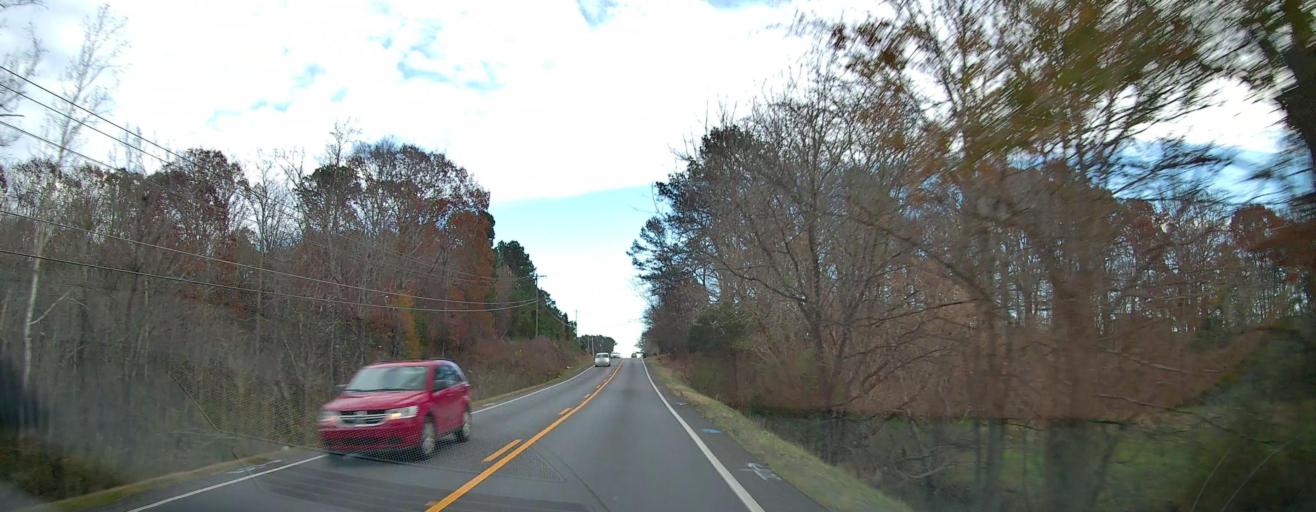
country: US
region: Alabama
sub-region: Morgan County
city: Priceville
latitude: 34.4531
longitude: -86.7672
